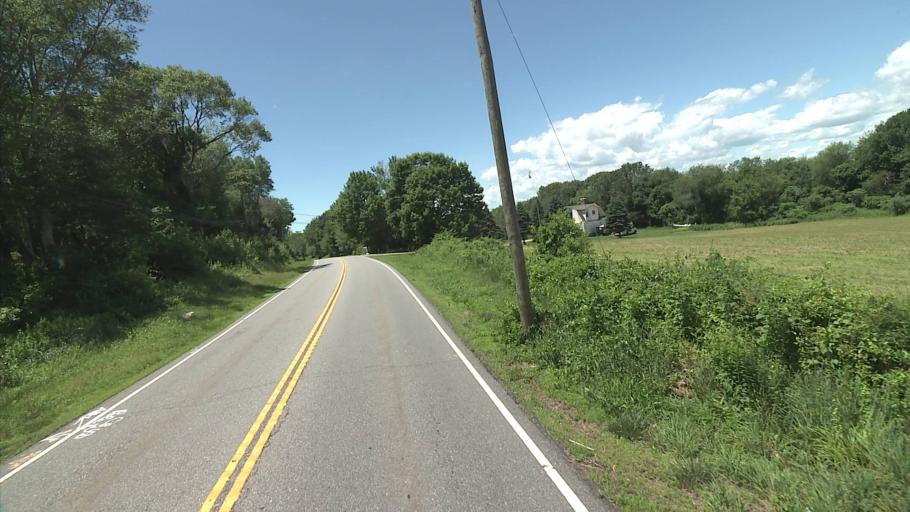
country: US
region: Connecticut
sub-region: New London County
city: Pawcatuck
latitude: 41.3812
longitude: -71.8932
